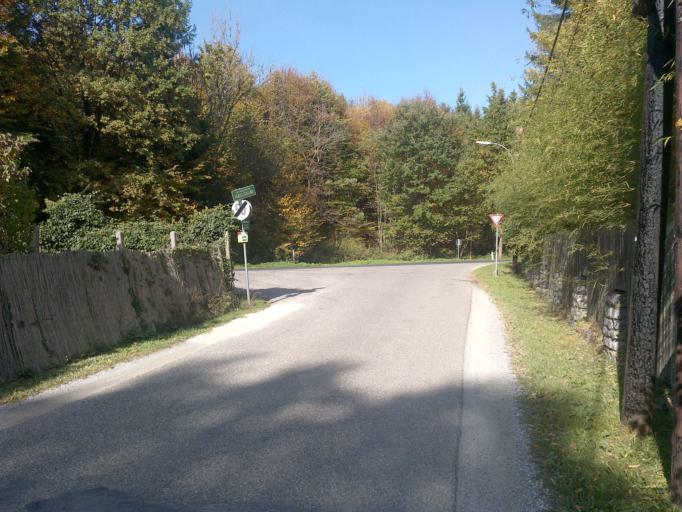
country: AT
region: Styria
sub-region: Politischer Bezirk Graz-Umgebung
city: Thal
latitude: 47.0474
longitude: 15.3618
